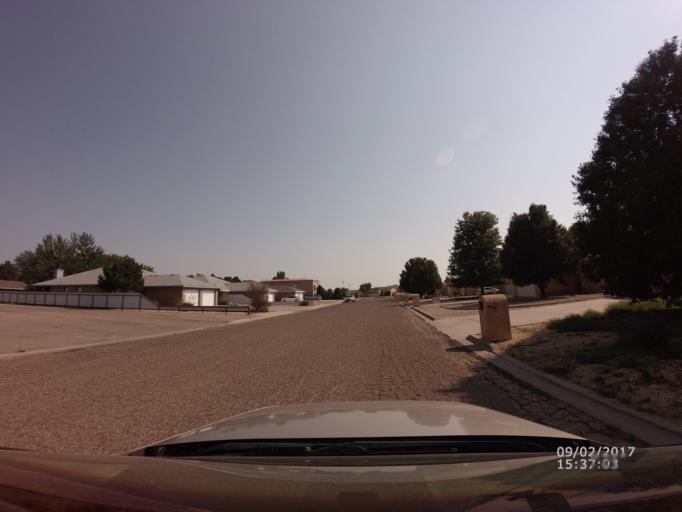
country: US
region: New Mexico
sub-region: Curry County
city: Clovis
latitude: 34.4376
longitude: -103.1944
